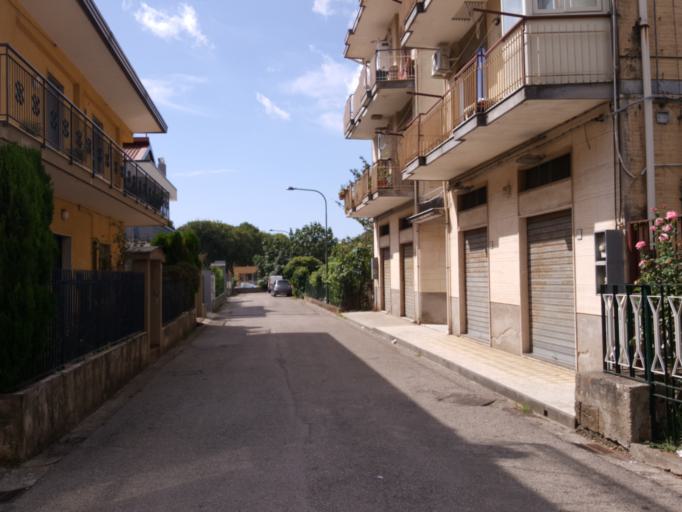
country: IT
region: Campania
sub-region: Provincia di Salerno
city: Baronissi
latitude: 40.7498
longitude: 14.7756
